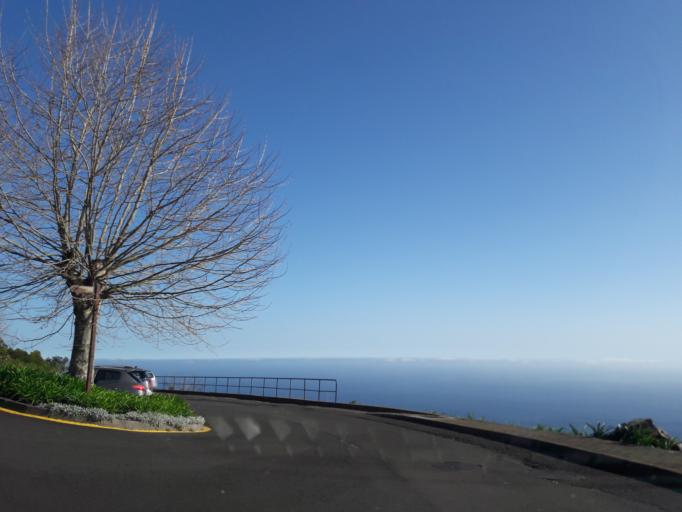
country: PT
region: Madeira
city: Canico
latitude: 32.6530
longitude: -16.8725
